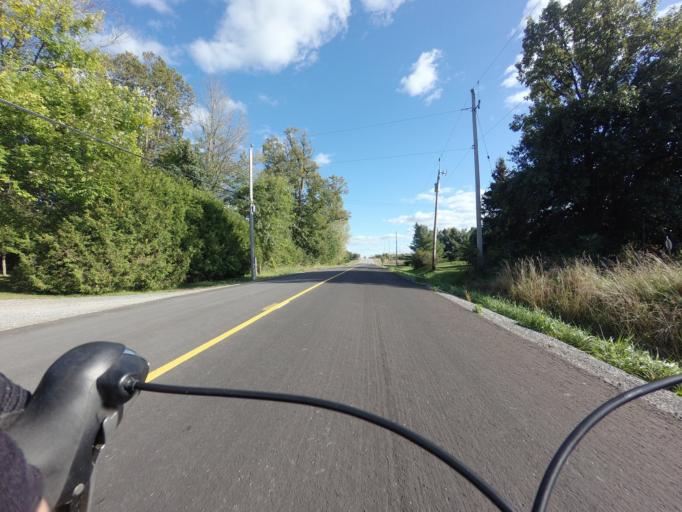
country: CA
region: Ontario
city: Bells Corners
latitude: 45.1282
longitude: -75.6779
